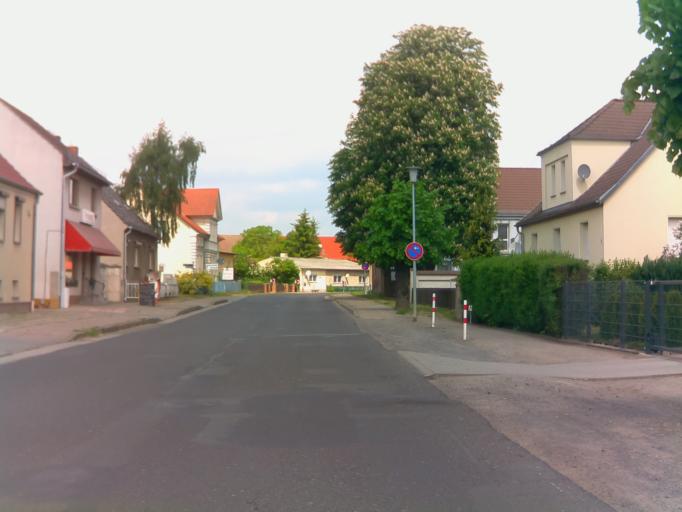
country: DE
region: Brandenburg
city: Retzow
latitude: 52.6257
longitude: 12.6847
